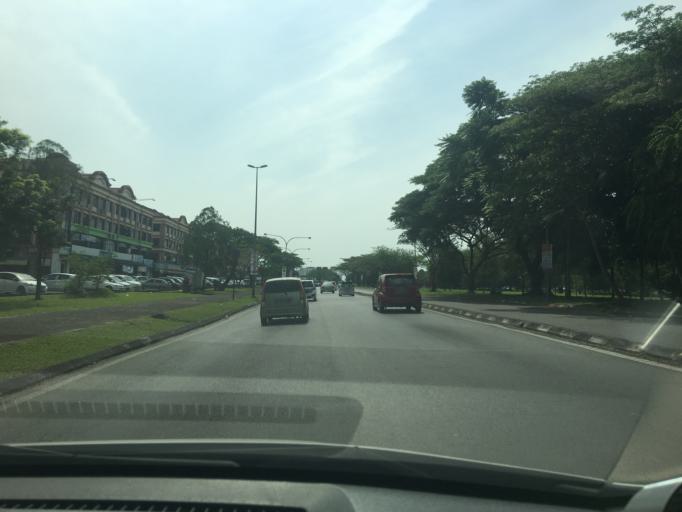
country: MY
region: Sarawak
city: Kuching
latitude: 1.5129
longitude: 110.3089
